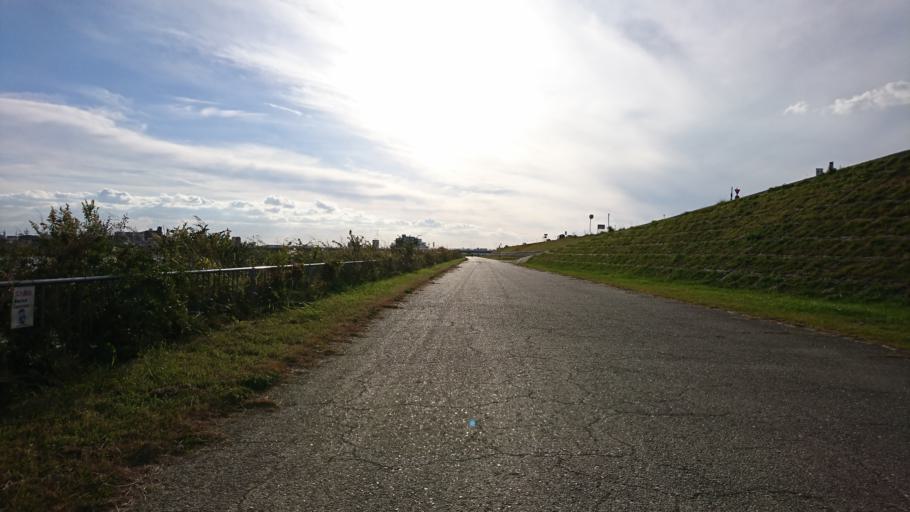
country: JP
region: Hyogo
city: Kakogawacho-honmachi
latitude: 34.7819
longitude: 134.8445
